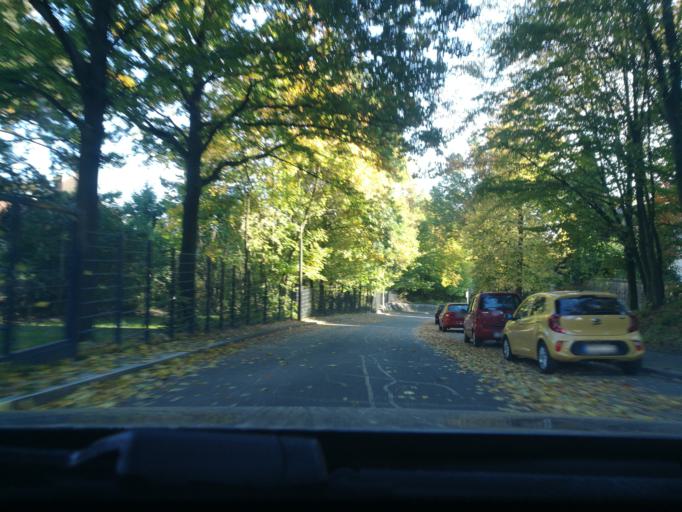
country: DE
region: Bavaria
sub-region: Regierungsbezirk Mittelfranken
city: Nuernberg
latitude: 49.4738
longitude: 11.1331
